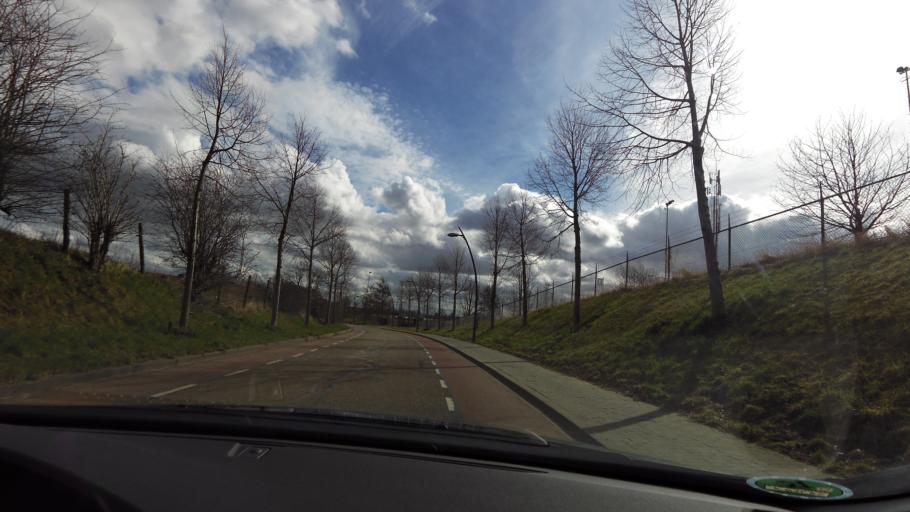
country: NL
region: Limburg
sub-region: Gemeente Nuth
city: Nuth
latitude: 50.9122
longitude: 5.8850
